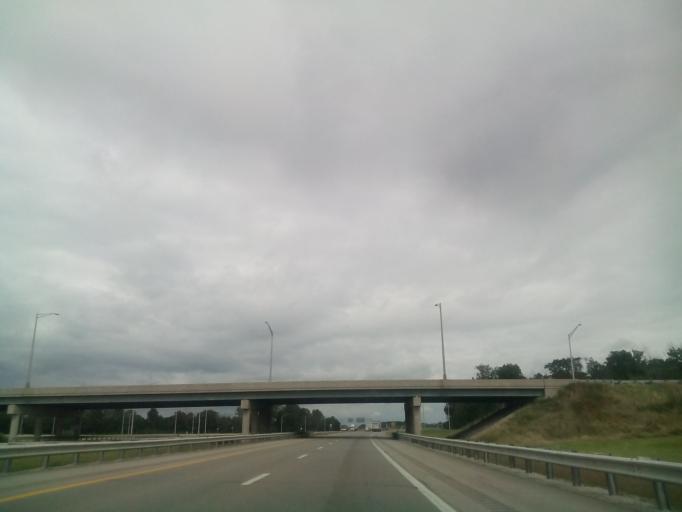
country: US
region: Ohio
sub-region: Fulton County
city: Burlington
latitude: 41.5914
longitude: -84.3213
